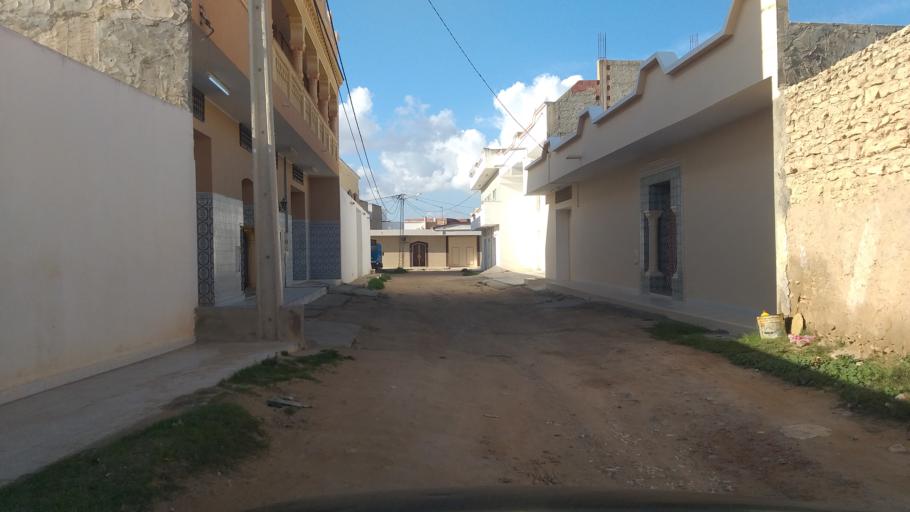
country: TN
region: Al Mahdiyah
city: El Jem
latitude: 35.2901
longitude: 10.7126
